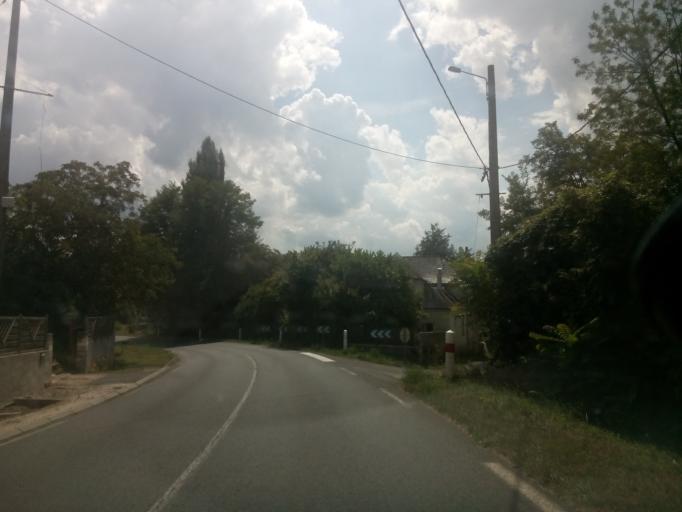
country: FR
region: Centre
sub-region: Departement d'Indre-et-Loire
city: Cheille
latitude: 47.2723
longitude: 0.4242
